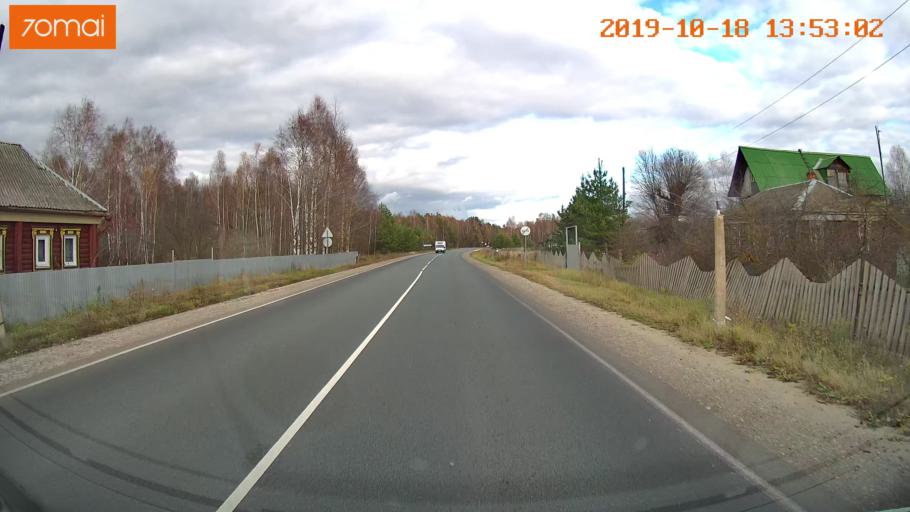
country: RU
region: Moskovskaya
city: Radovitskiy
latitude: 55.0347
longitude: 39.9740
